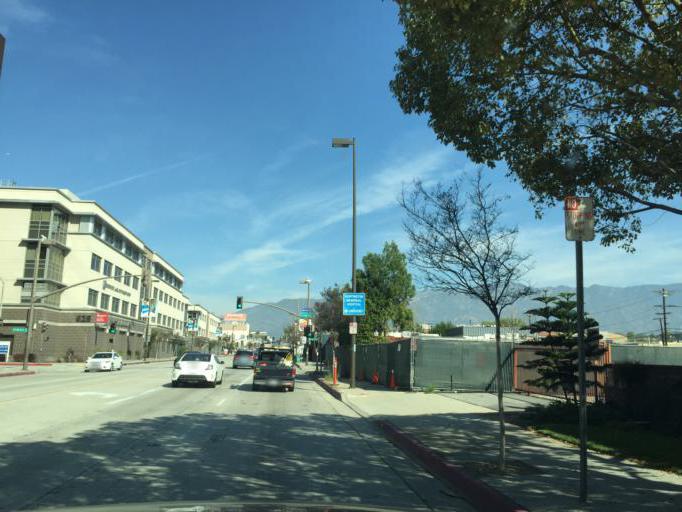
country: US
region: California
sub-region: Los Angeles County
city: Pasadena
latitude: 34.1336
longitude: -118.1503
